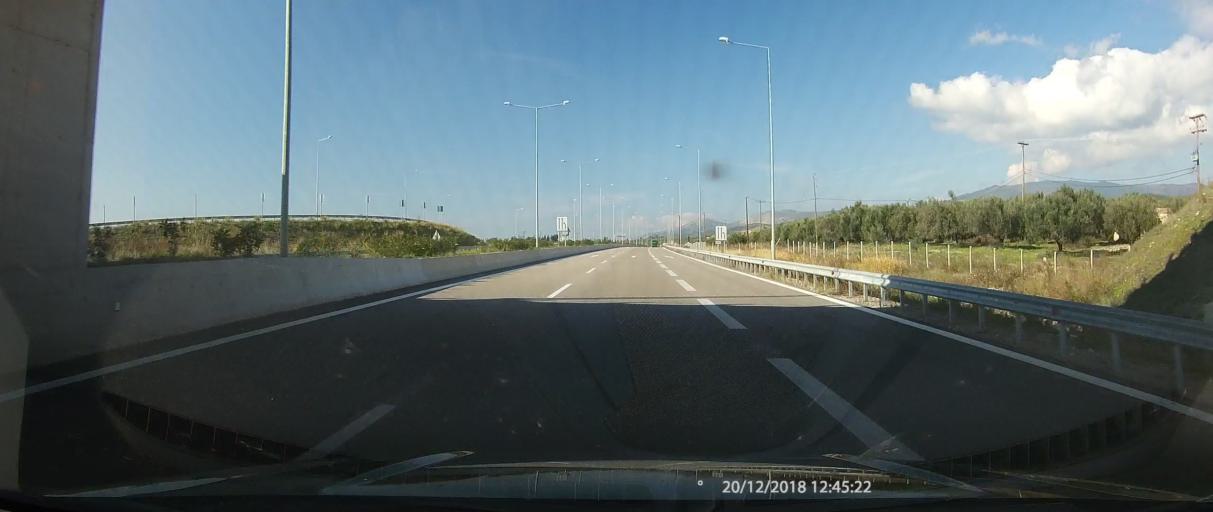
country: GR
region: West Greece
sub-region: Nomos Aitolias kai Akarnanias
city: Mesolongi
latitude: 38.3800
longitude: 21.4983
